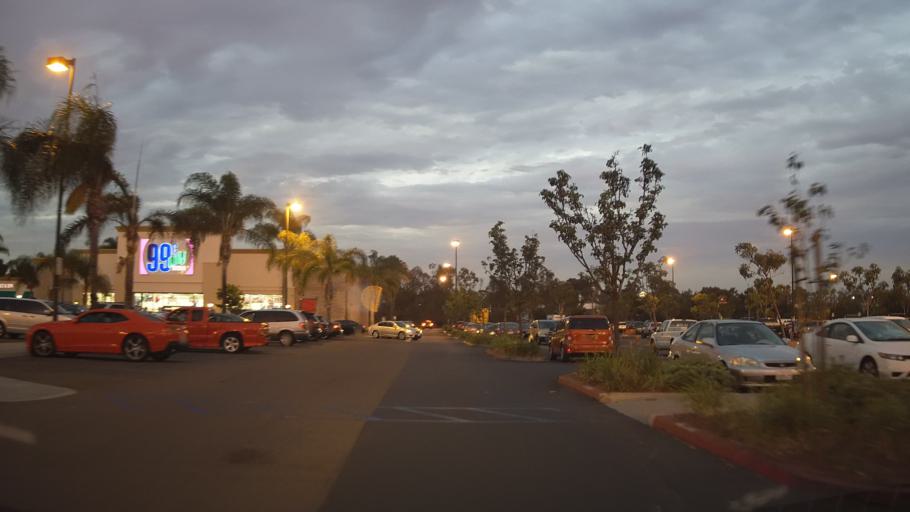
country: US
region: California
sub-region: San Diego County
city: National City
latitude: 32.7032
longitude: -117.1013
